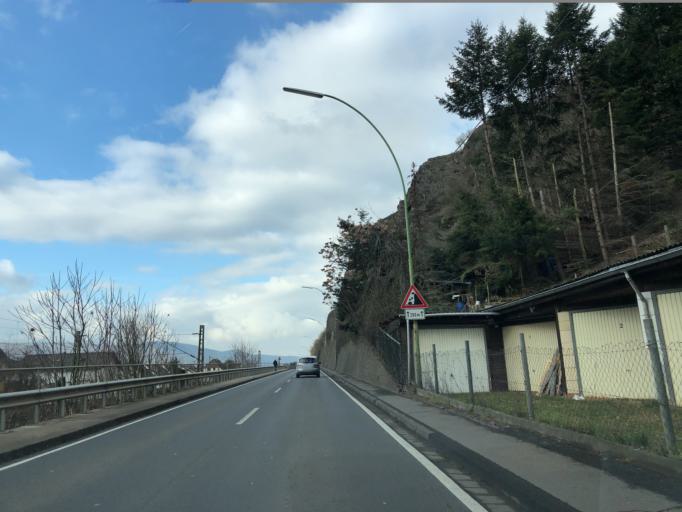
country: DE
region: Rheinland-Pfalz
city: Braubach
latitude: 50.2781
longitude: 7.6399
